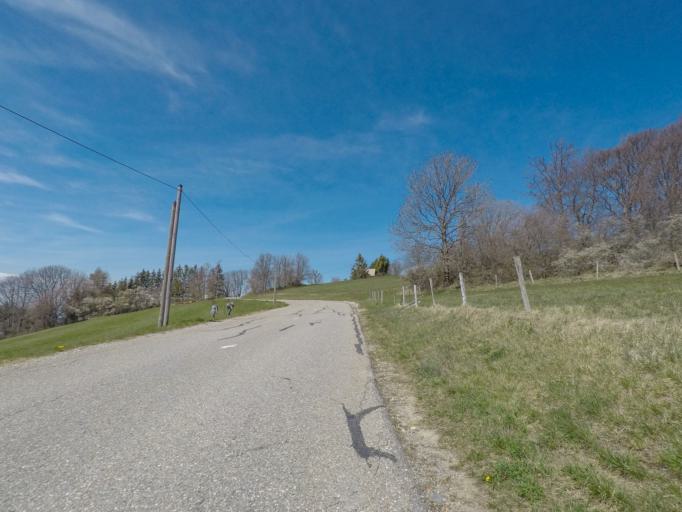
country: FR
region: Rhone-Alpes
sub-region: Departement de la Haute-Savoie
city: Collonges-sous-Saleve
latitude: 46.1214
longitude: 6.1713
